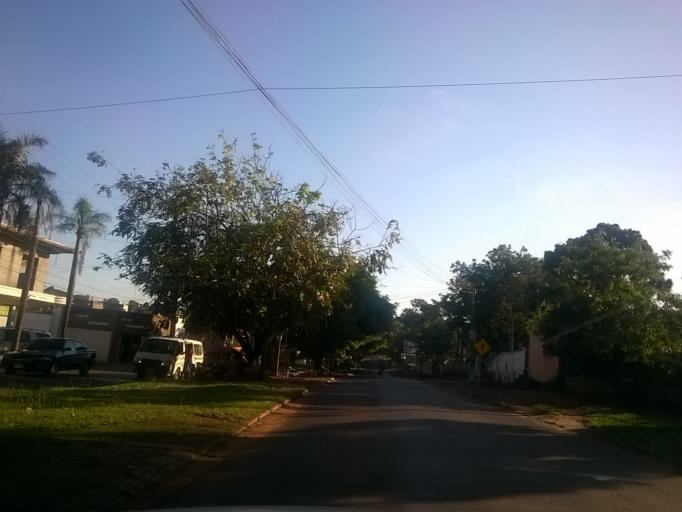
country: PY
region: Alto Parana
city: Ciudad del Este
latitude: -25.5029
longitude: -54.6283
